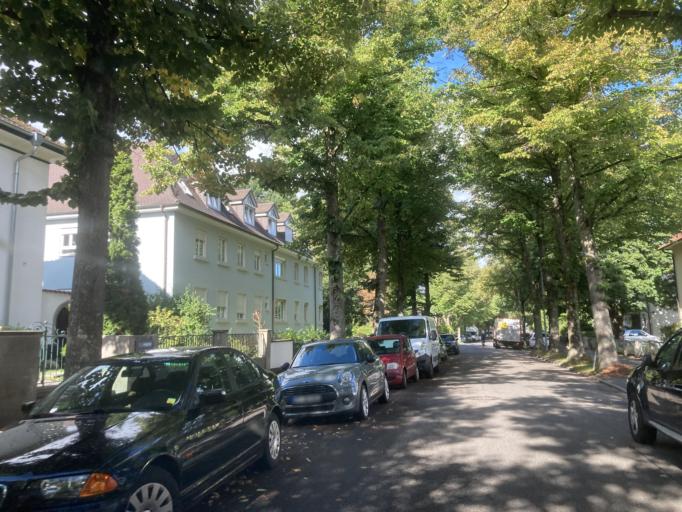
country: DE
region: Baden-Wuerttemberg
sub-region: Freiburg Region
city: Freiburg
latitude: 48.0096
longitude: 7.8607
